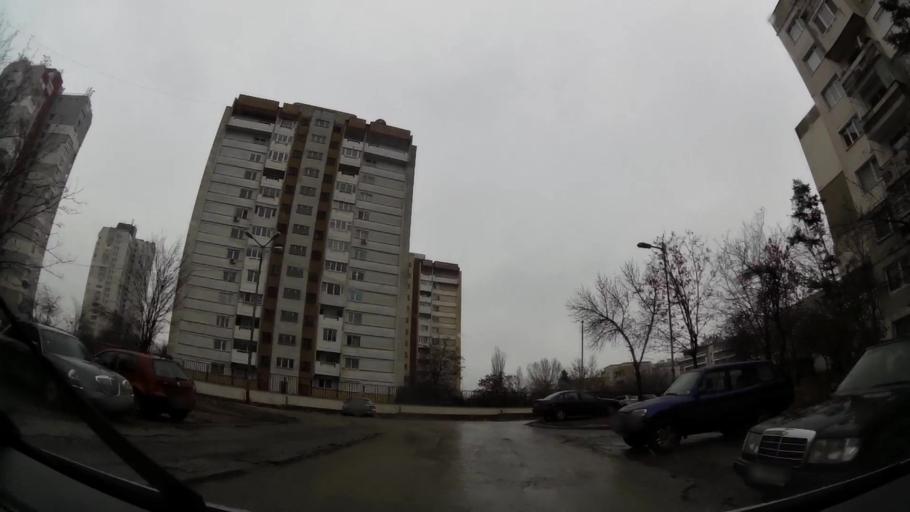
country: BG
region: Sofia-Capital
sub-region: Stolichna Obshtina
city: Sofia
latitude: 42.6401
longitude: 23.3676
